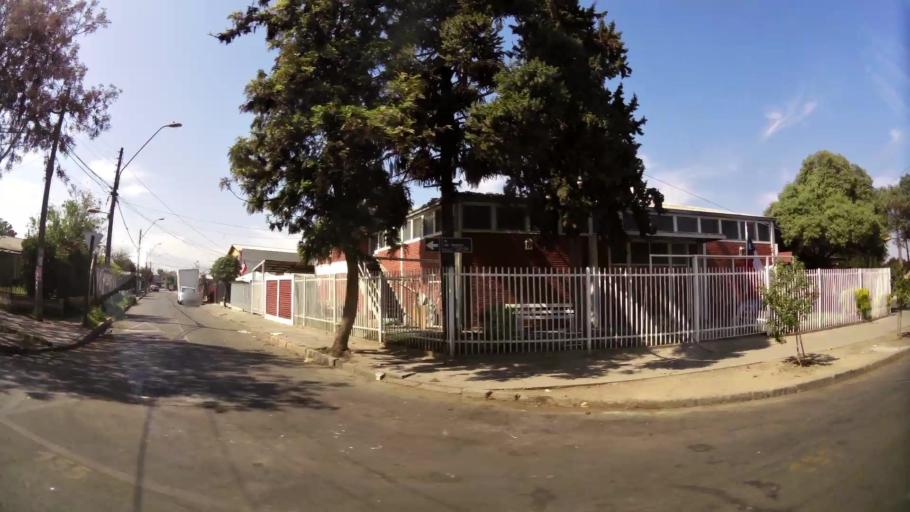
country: CL
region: Santiago Metropolitan
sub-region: Provincia de Santiago
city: Lo Prado
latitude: -33.4741
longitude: -70.7308
